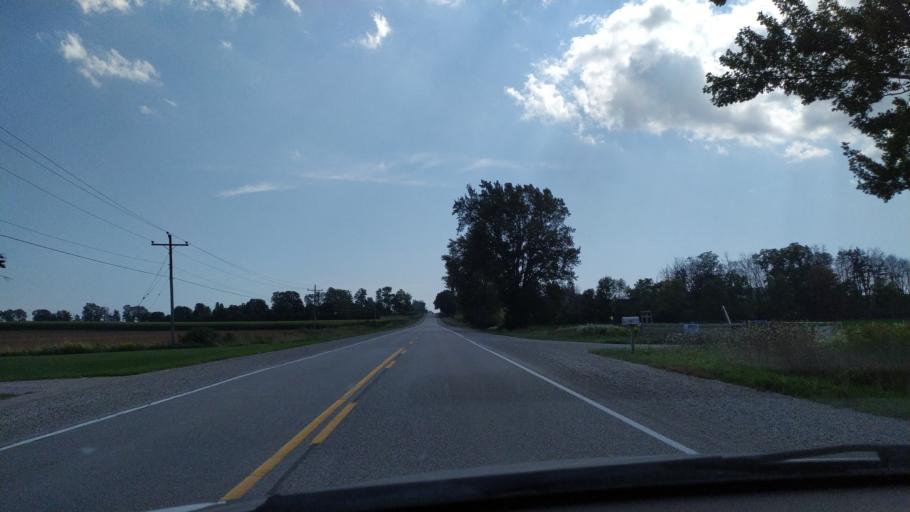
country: CA
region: Ontario
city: Ingersoll
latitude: 43.1330
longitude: -80.8898
